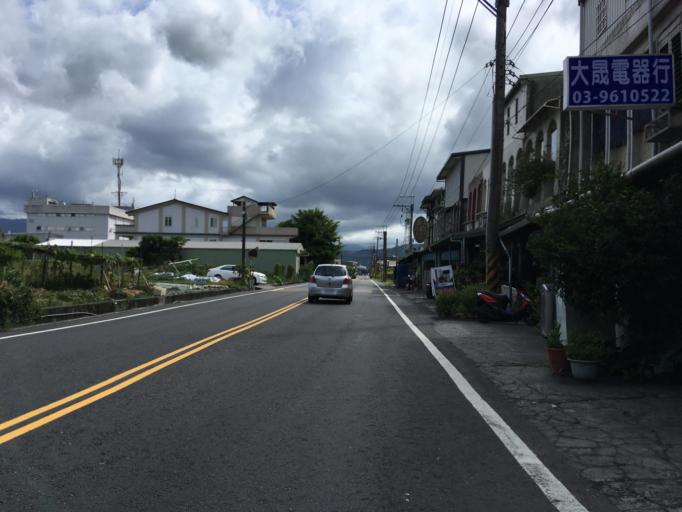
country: TW
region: Taiwan
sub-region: Yilan
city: Yilan
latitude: 24.6687
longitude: 121.7474
